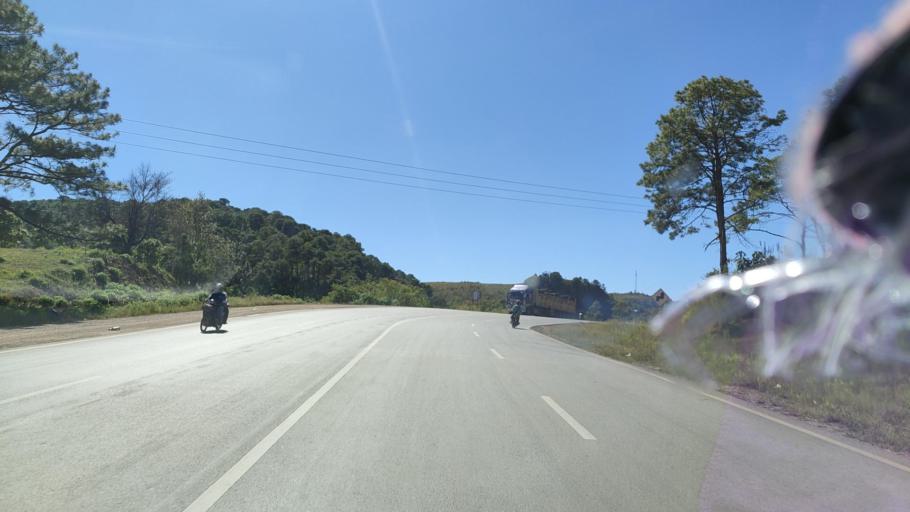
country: MM
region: Shan
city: Taunggyi
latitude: 20.6469
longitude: 96.6128
